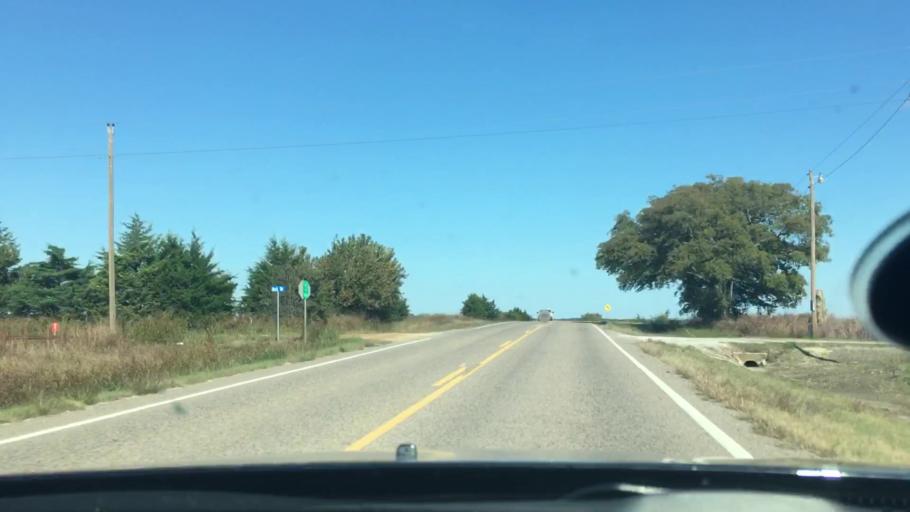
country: US
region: Oklahoma
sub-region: Johnston County
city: Tishomingo
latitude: 34.1576
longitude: -96.7059
